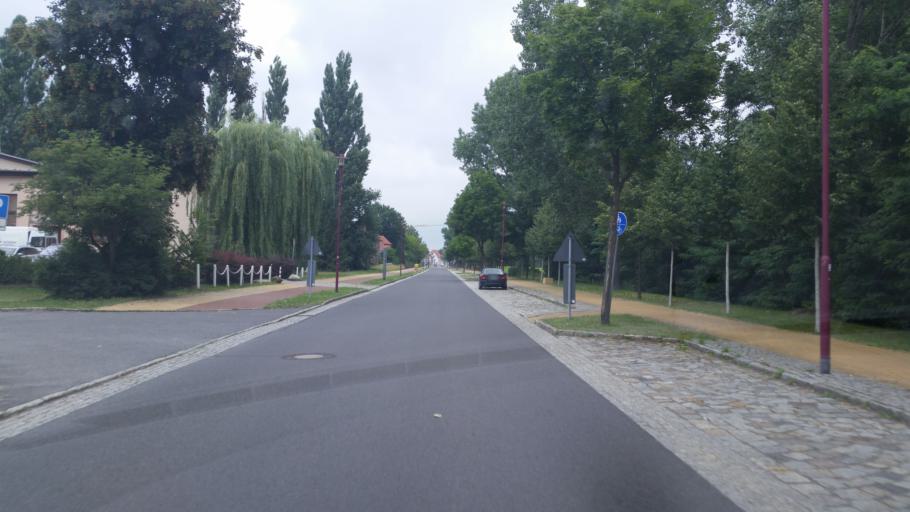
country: DE
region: Brandenburg
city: Grossraschen
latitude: 51.5805
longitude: 14.0103
